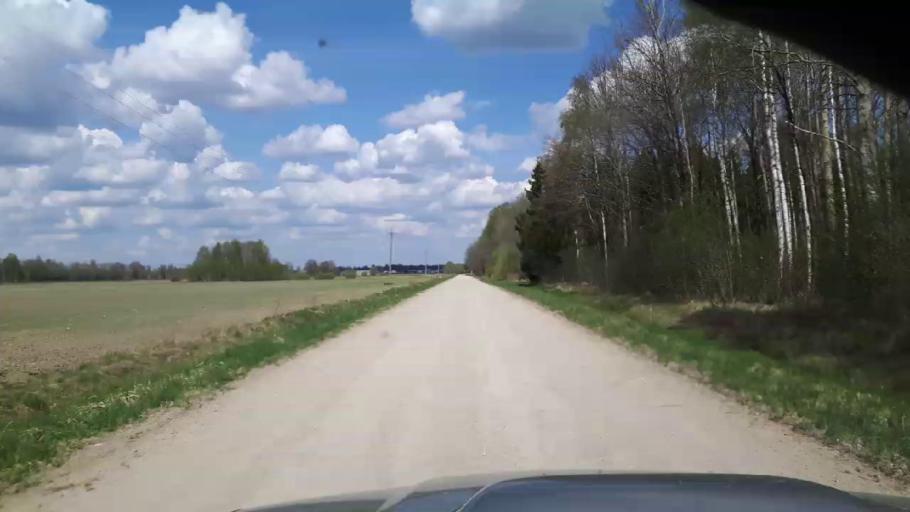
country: EE
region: Paernumaa
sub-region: Tootsi vald
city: Tootsi
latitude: 58.4793
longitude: 24.9021
